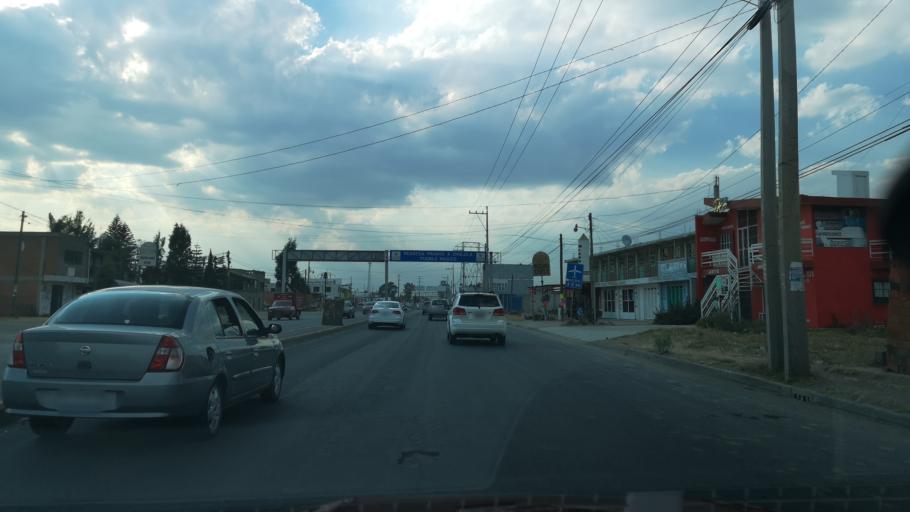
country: MX
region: Puebla
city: Cholula
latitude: 19.0763
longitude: -98.3218
